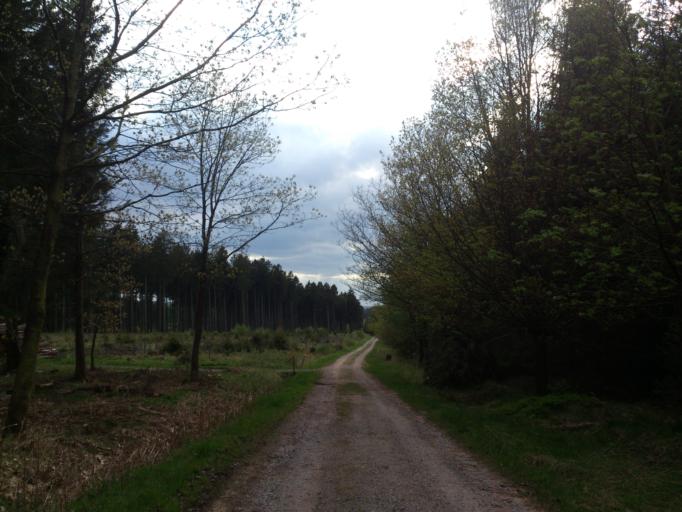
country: DE
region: North Rhine-Westphalia
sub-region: Regierungsbezirk Detmold
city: Willebadessen
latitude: 51.5983
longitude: 9.0078
